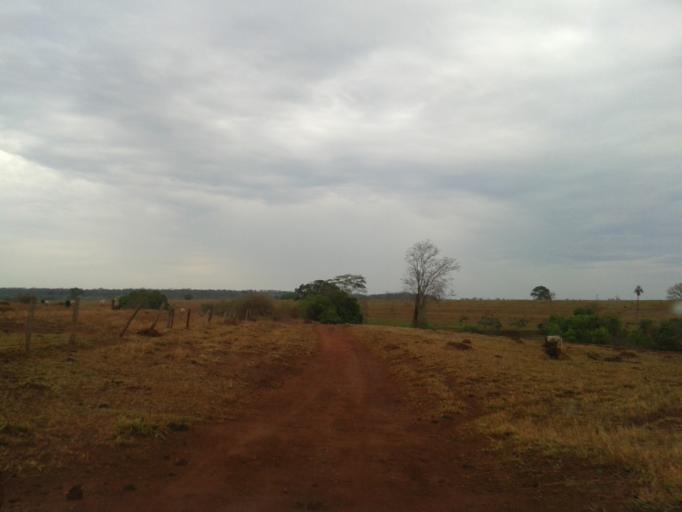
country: BR
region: Minas Gerais
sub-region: Santa Vitoria
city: Santa Vitoria
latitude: -18.8608
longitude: -49.8266
